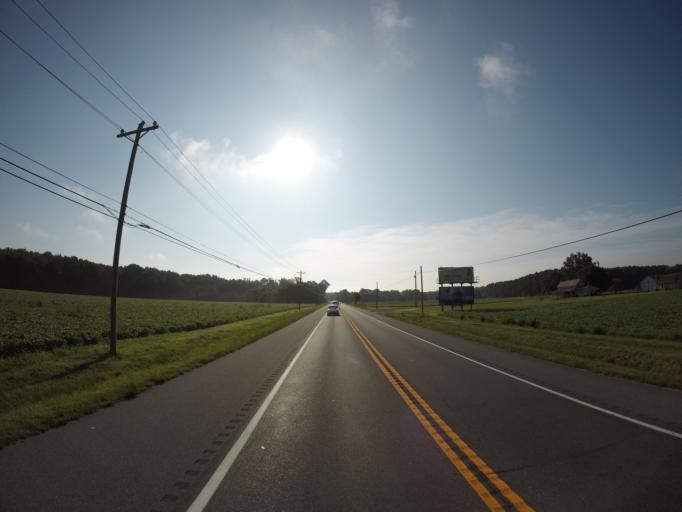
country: US
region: Delaware
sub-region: Sussex County
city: Georgetown
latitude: 38.6987
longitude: -75.4483
